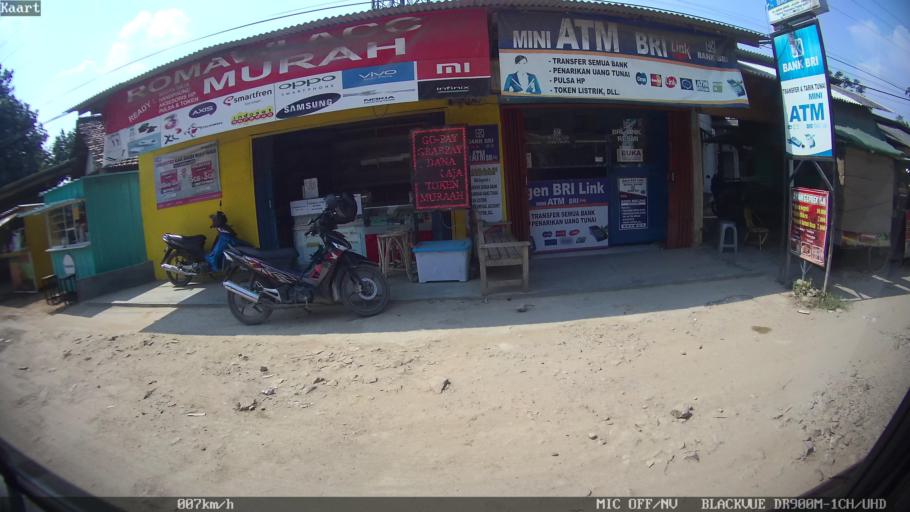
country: ID
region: Lampung
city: Natar
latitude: -5.3099
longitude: 105.2090
